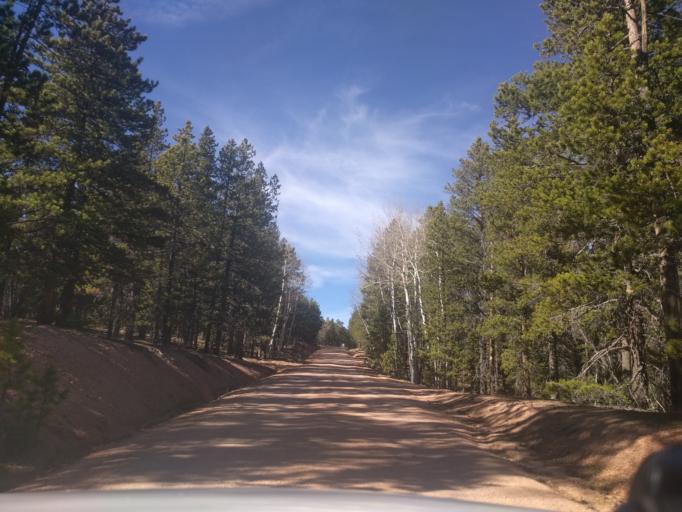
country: US
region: Colorado
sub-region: Douglas County
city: Perry Park
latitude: 39.1889
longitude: -105.0492
